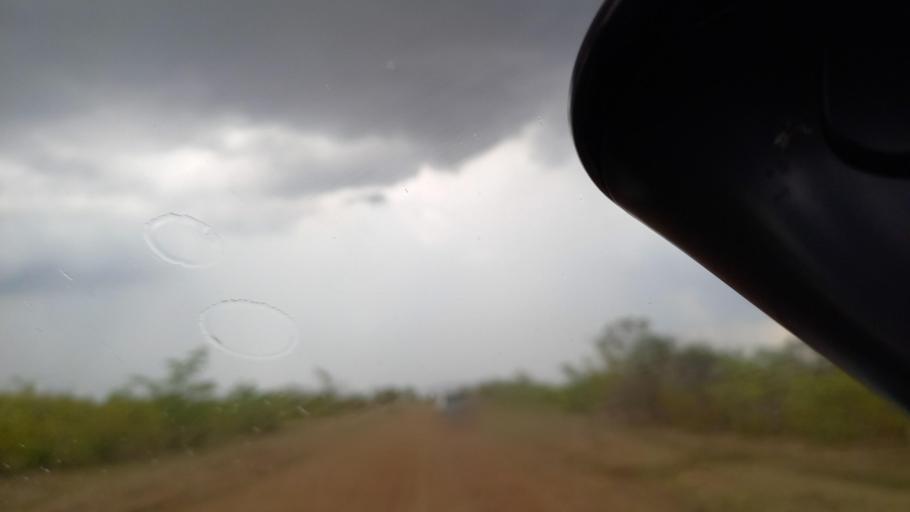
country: ZM
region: Lusaka
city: Kafue
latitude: -15.8656
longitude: 28.1825
